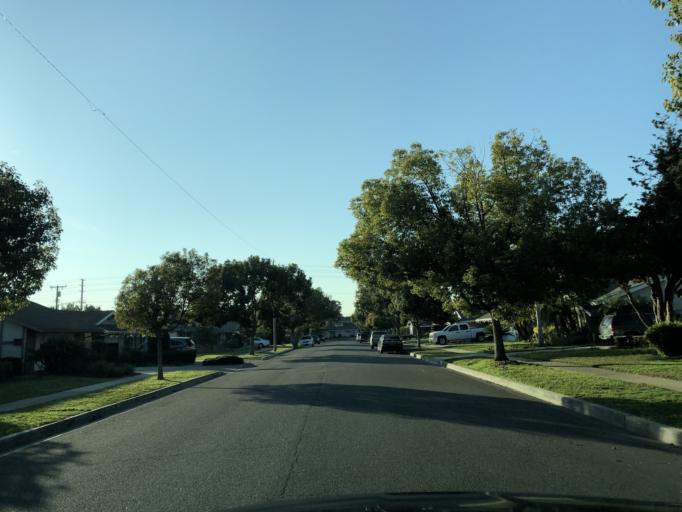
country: US
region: California
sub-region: Orange County
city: Orange
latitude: 33.7639
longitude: -117.8455
